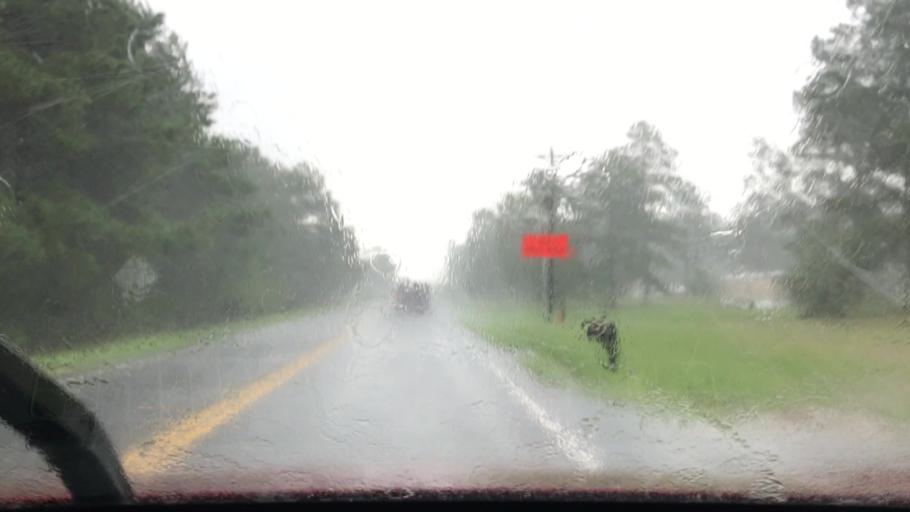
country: US
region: South Carolina
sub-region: Horry County
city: Loris
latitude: 33.9012
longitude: -78.8734
